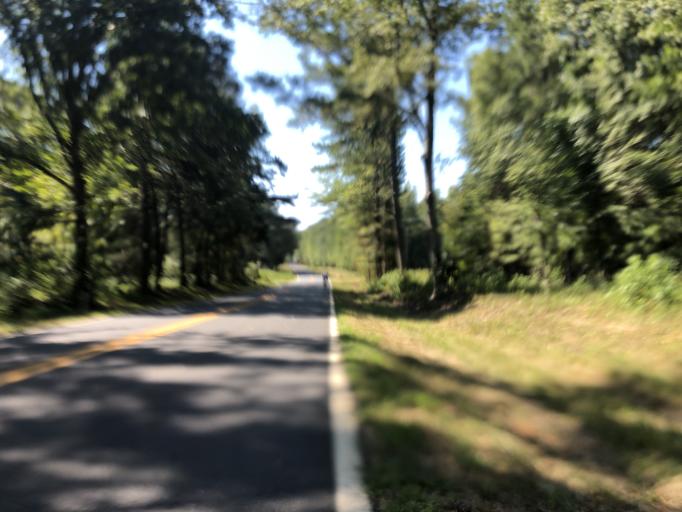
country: US
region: Georgia
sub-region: Heard County
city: Franklin
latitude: 33.3811
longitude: -84.9688
